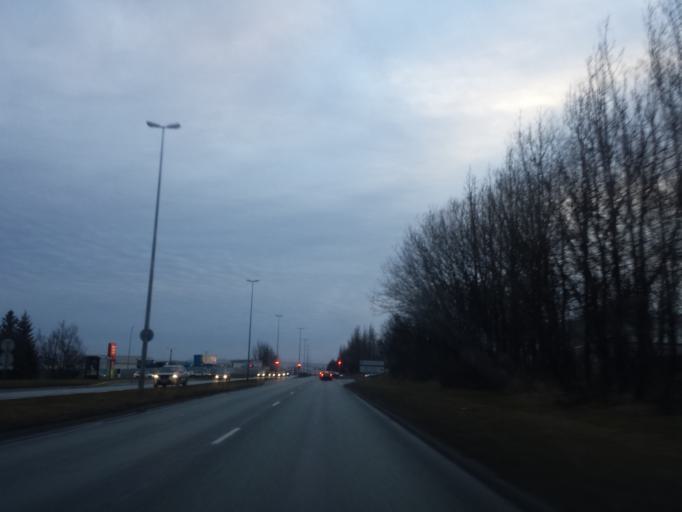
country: IS
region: Capital Region
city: Reykjavik
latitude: 64.1356
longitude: -21.8503
